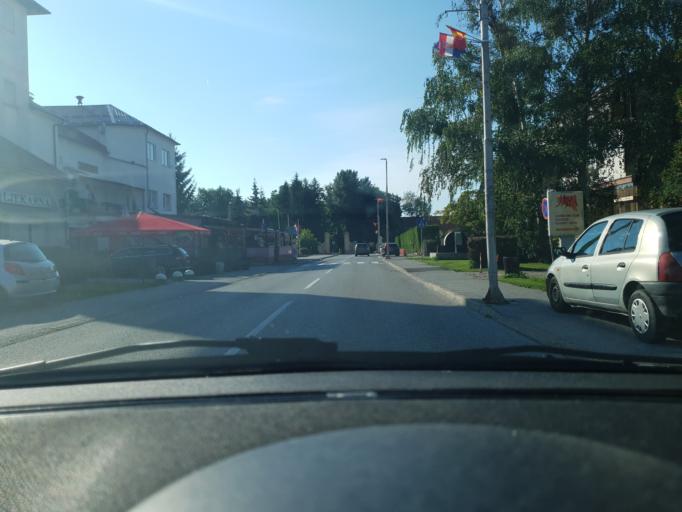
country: HR
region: Krapinsko-Zagorska
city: Oroslavje
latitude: 45.9959
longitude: 15.9155
